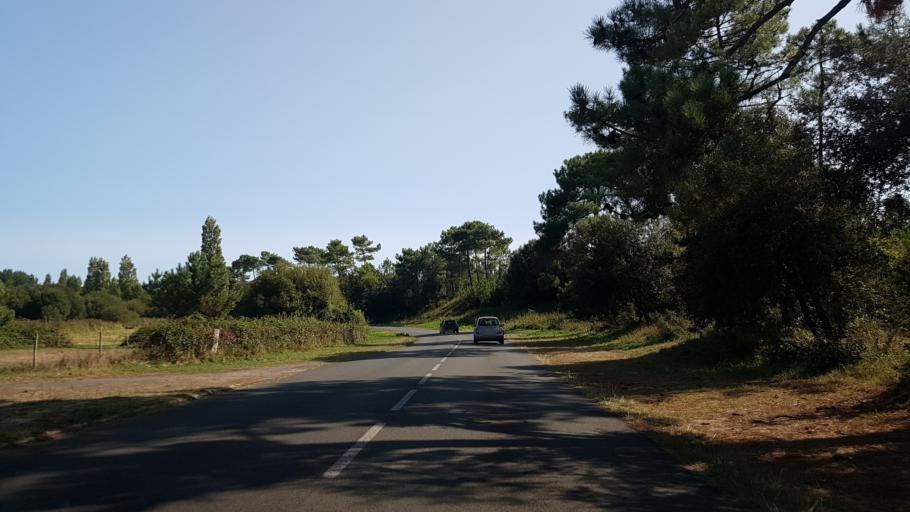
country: FR
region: Poitou-Charentes
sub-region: Departement de la Charente-Maritime
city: Les Mathes
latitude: 45.6963
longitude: -1.1954
